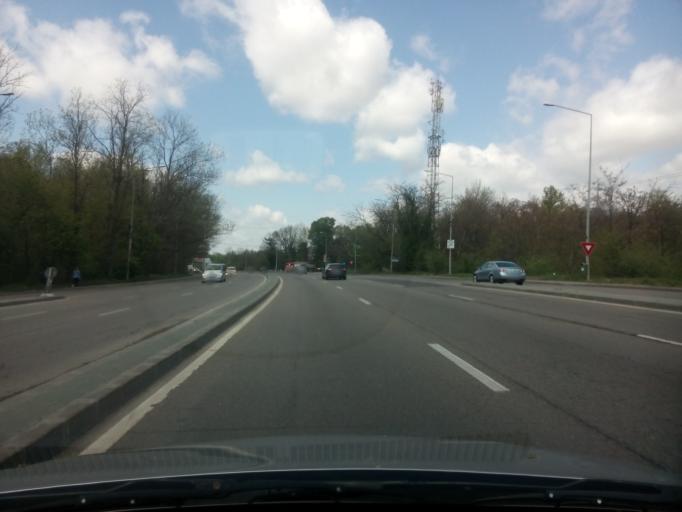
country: RO
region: Ilfov
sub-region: Comuna Otopeni
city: Otopeni
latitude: 44.5164
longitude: 26.0794
